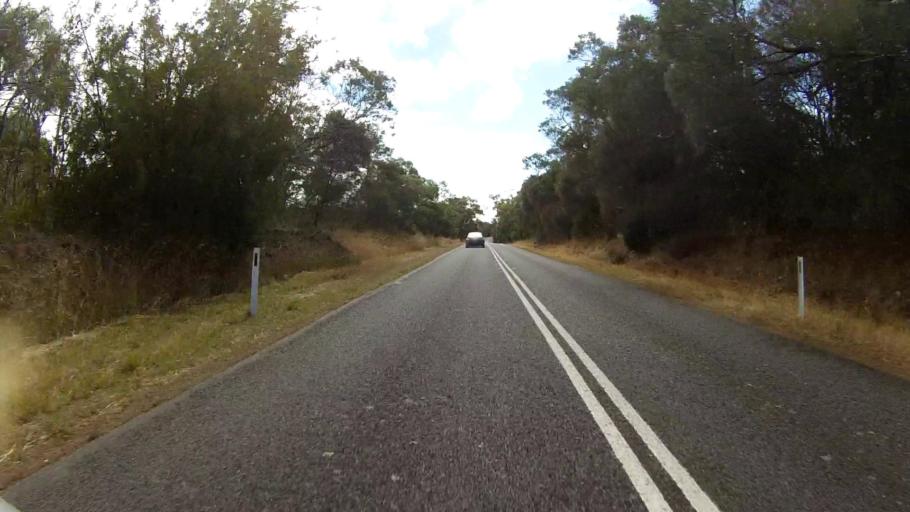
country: AU
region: Tasmania
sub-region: Sorell
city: Sorell
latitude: -42.1495
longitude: 148.0682
